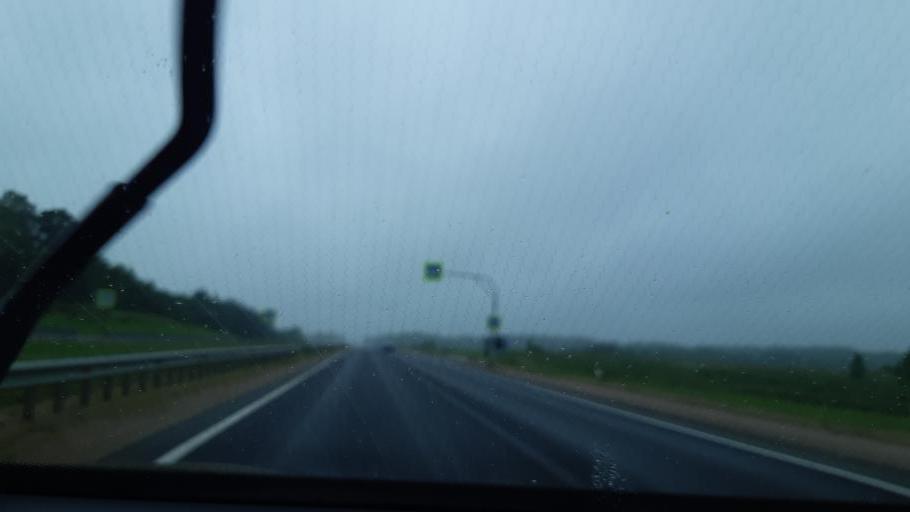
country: RU
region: Smolensk
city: Talashkino
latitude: 54.6269
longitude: 32.1896
